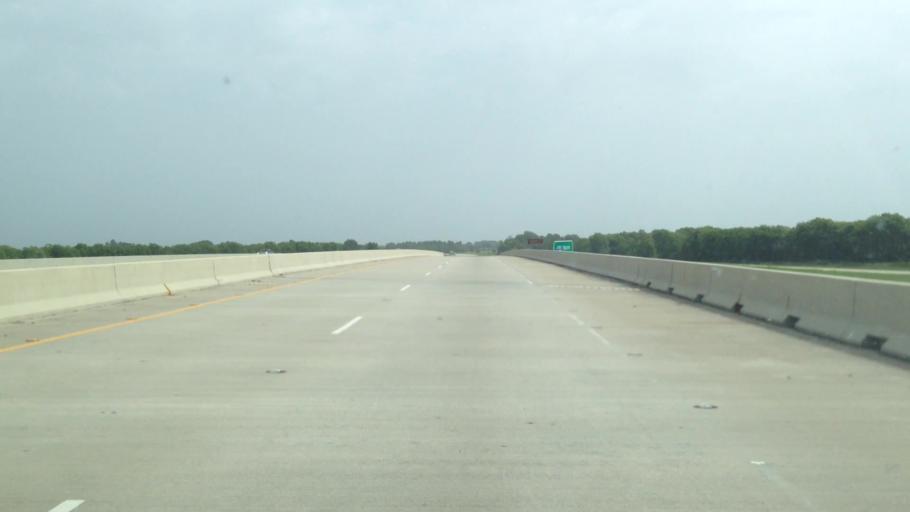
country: US
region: Louisiana
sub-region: Caddo Parish
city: Vivian
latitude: 32.8510
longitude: -93.8647
